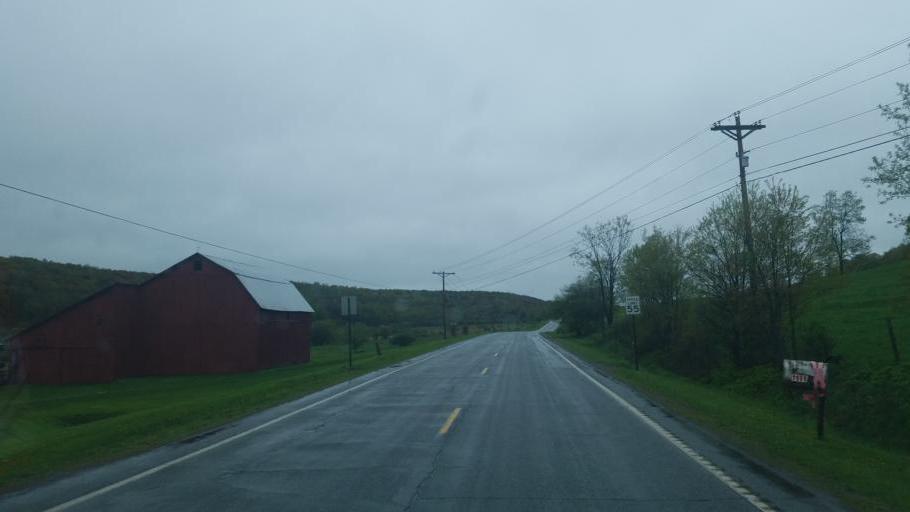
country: US
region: Pennsylvania
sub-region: Potter County
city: Coudersport
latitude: 41.8690
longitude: -77.8419
